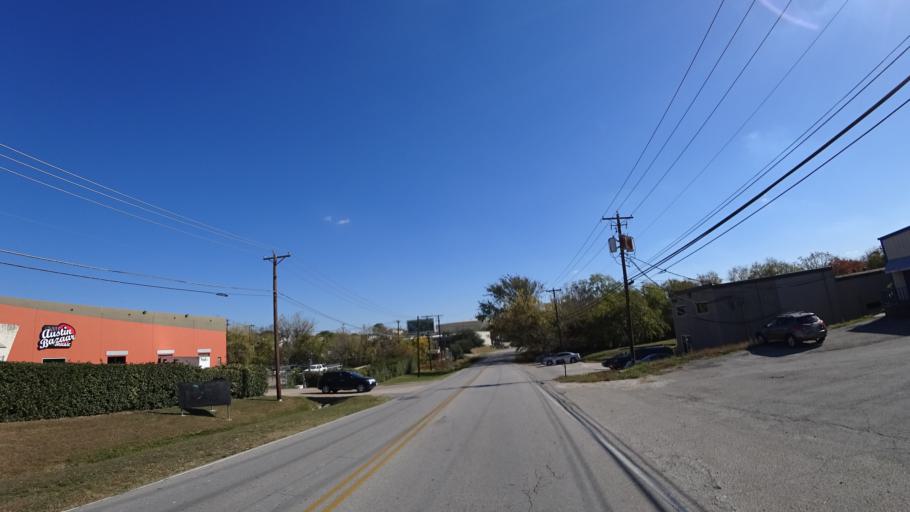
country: US
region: Texas
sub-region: Travis County
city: Wells Branch
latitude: 30.4353
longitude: -97.6876
